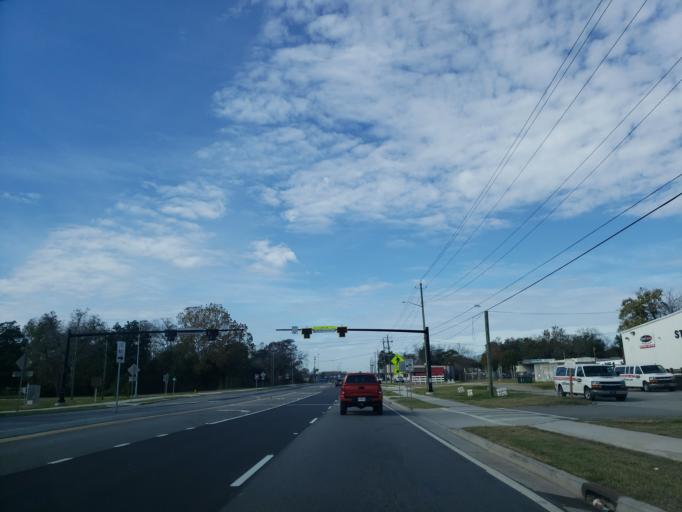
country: US
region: Georgia
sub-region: Chatham County
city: Savannah
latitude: 32.0885
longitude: -81.1193
